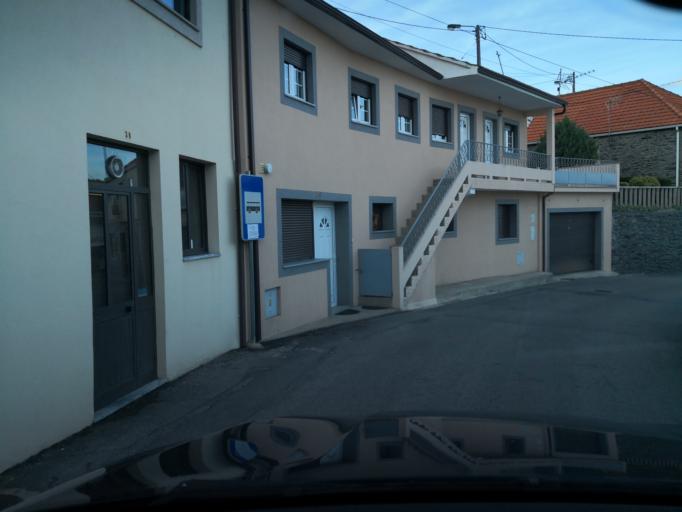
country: PT
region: Vila Real
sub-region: Santa Marta de Penaguiao
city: Santa Marta de Penaguiao
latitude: 41.2282
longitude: -7.8177
